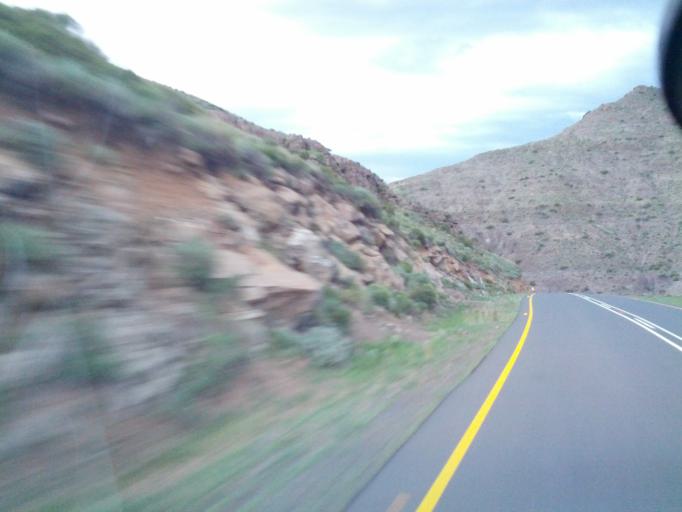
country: LS
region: Qacha's Nek
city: Qacha's Nek
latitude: -30.0409
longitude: 28.3087
